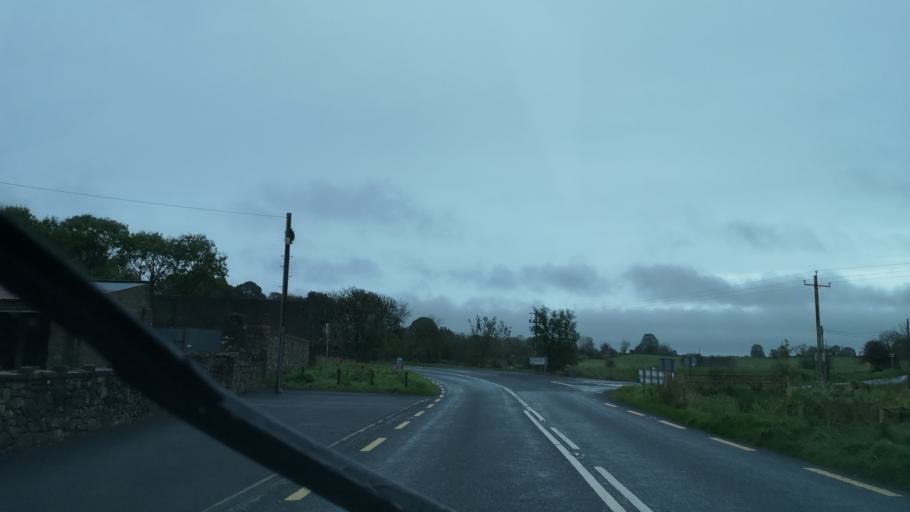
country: IE
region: Connaught
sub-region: Maigh Eo
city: Ballyhaunis
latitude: 53.7703
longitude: -8.7622
